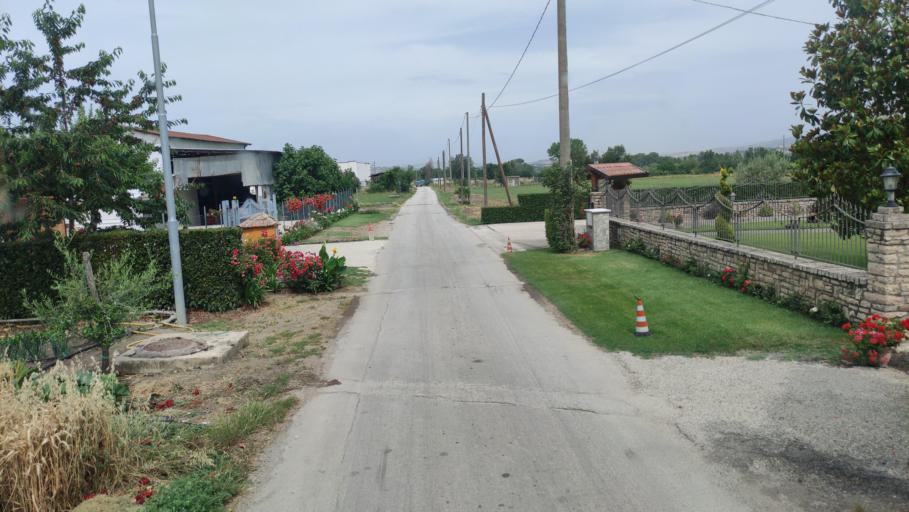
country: IT
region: Campania
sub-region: Provincia di Avellino
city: Sturno
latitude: 41.0507
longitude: 15.1250
